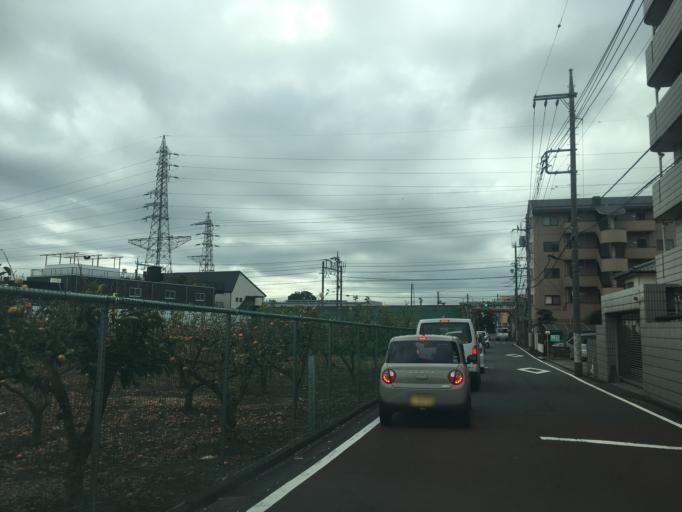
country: JP
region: Tokyo
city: Hino
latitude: 35.7291
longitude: 139.3862
